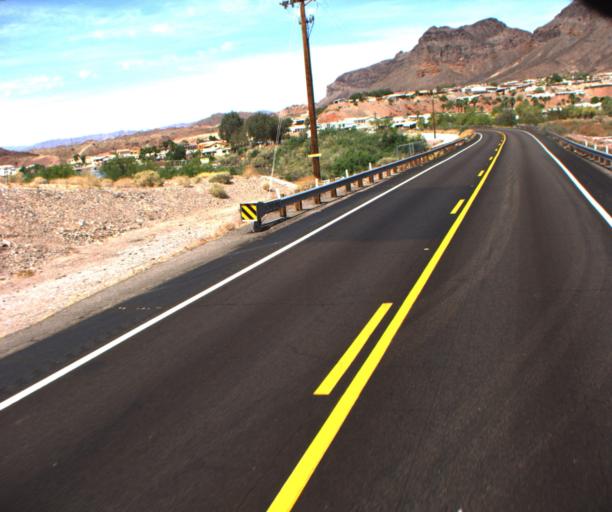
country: US
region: Arizona
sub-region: La Paz County
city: Cienega Springs
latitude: 34.2575
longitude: -114.1311
